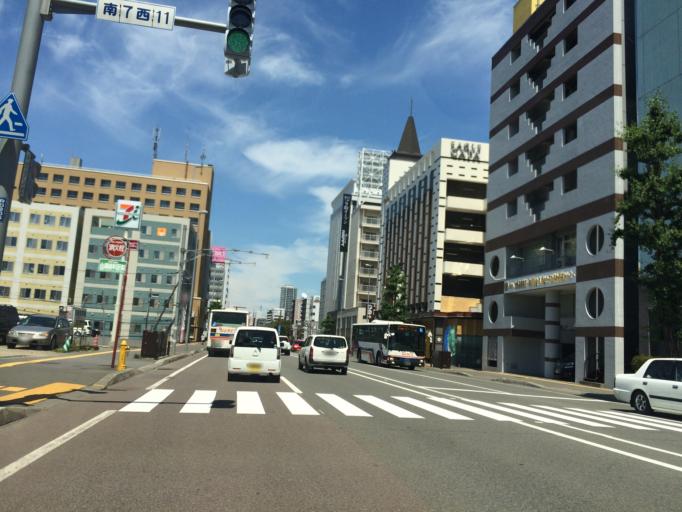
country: JP
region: Hokkaido
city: Sapporo
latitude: 43.0503
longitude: 141.3424
